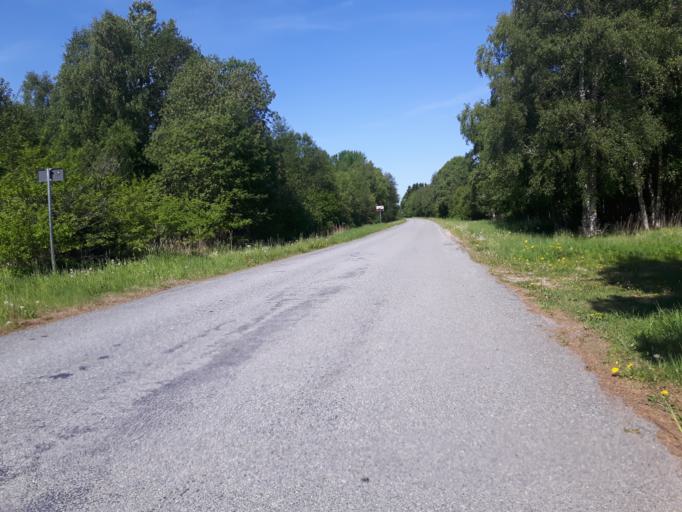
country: EE
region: Ida-Virumaa
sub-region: Aseri vald
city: Aseri
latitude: 59.4513
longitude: 26.8554
